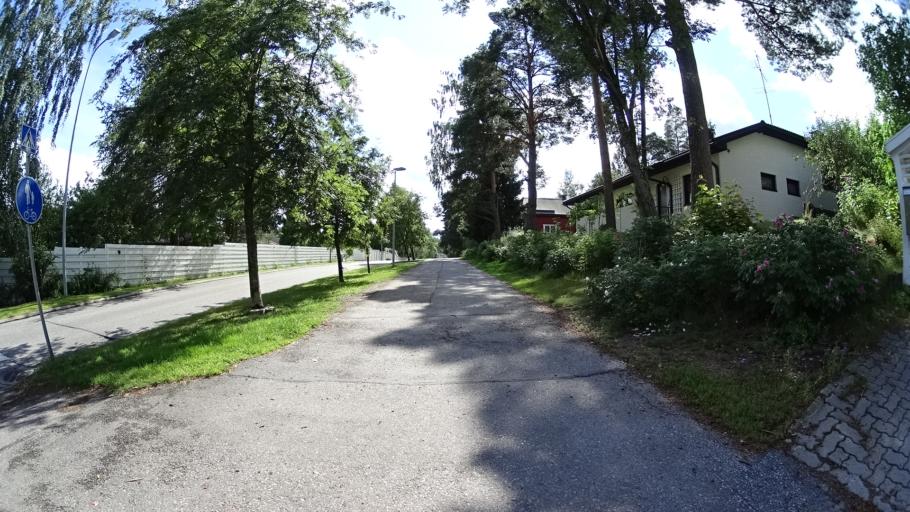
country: FI
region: Uusimaa
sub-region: Helsinki
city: Kilo
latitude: 60.1891
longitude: 24.7730
